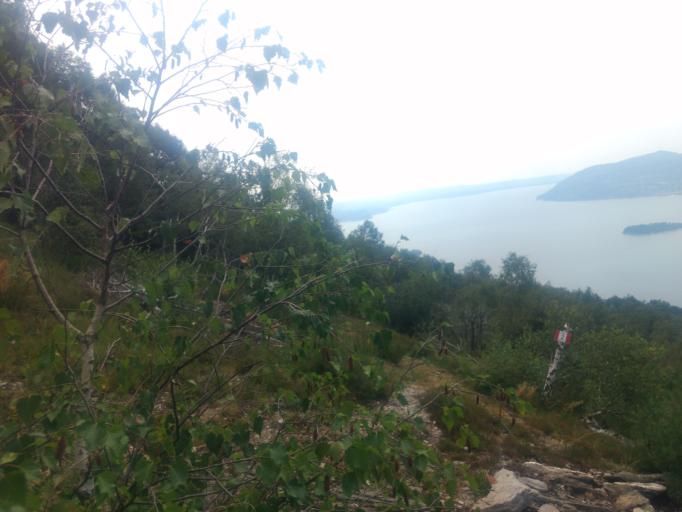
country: IT
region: Piedmont
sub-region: Provincia Verbano-Cusio-Ossola
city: Santino
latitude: 45.9451
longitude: 8.5319
